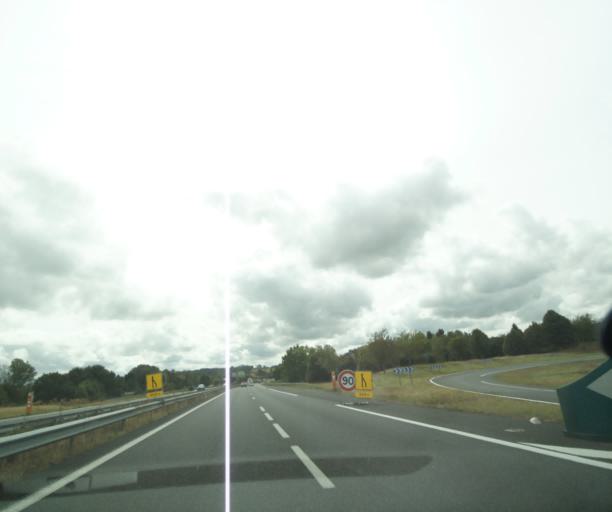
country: FR
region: Poitou-Charentes
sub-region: Departement de la Charente-Maritime
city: Mirambeau
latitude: 45.3707
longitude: -0.5928
